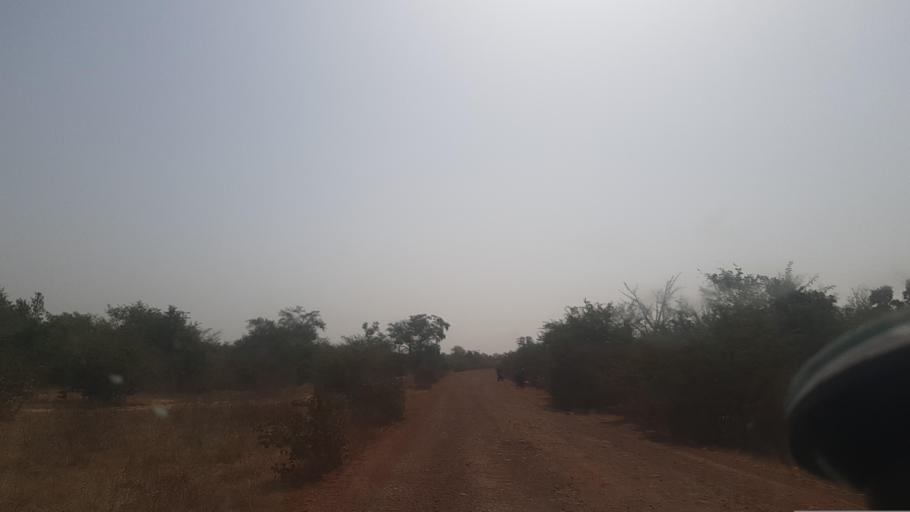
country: ML
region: Segou
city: Baroueli
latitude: 13.0652
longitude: -6.4764
